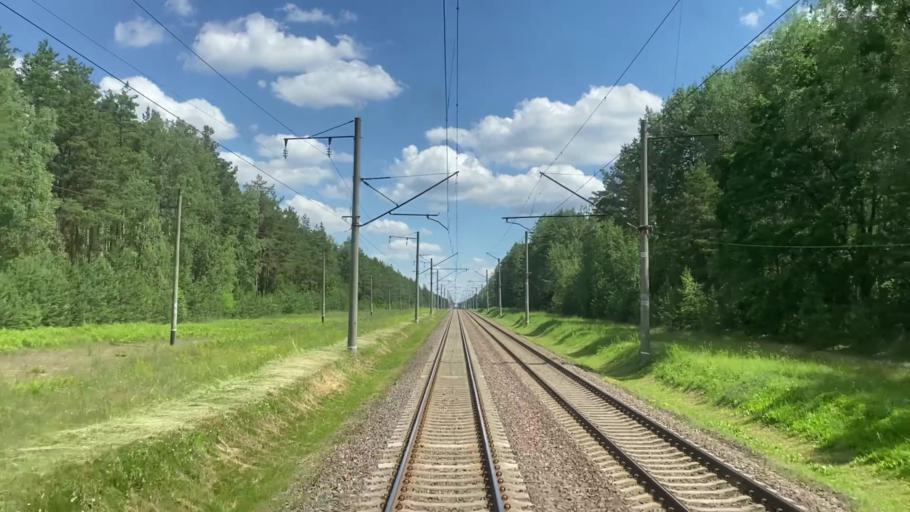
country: BY
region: Grodnenskaya
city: Zhyrovichy
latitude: 52.8620
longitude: 25.5902
